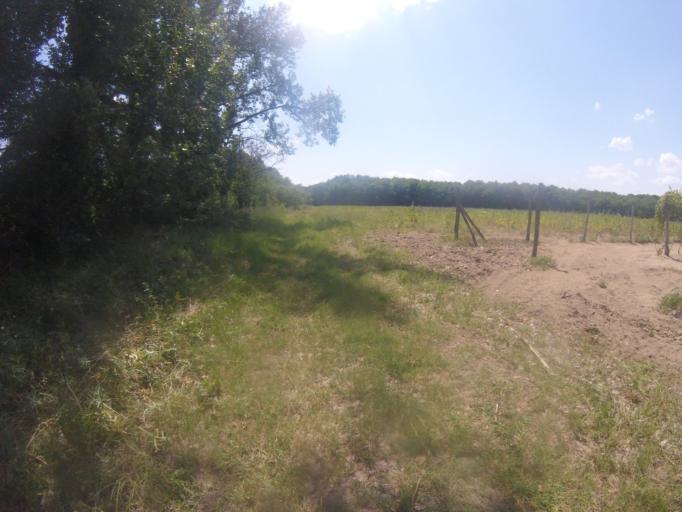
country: HU
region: Bacs-Kiskun
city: Jaszszentlaszlo
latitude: 46.6038
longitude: 19.7115
